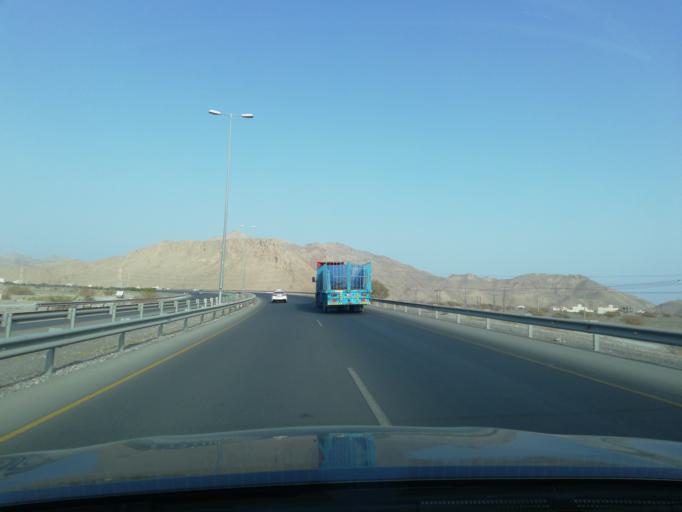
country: OM
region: Muhafazat ad Dakhiliyah
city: Nizwa
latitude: 22.8614
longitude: 57.5878
